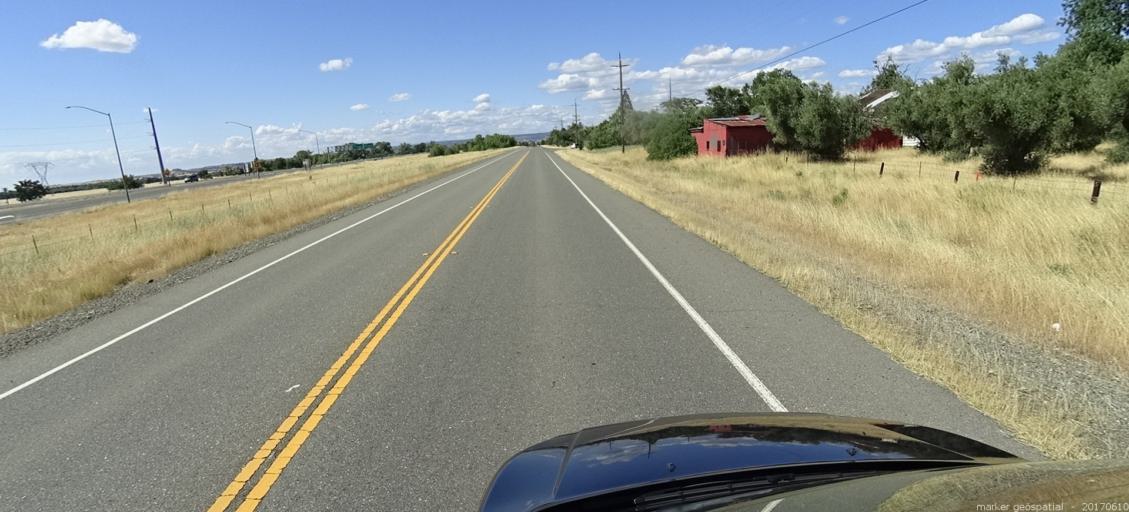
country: US
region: California
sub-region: Butte County
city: Thermalito
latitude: 39.5910
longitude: -121.6194
